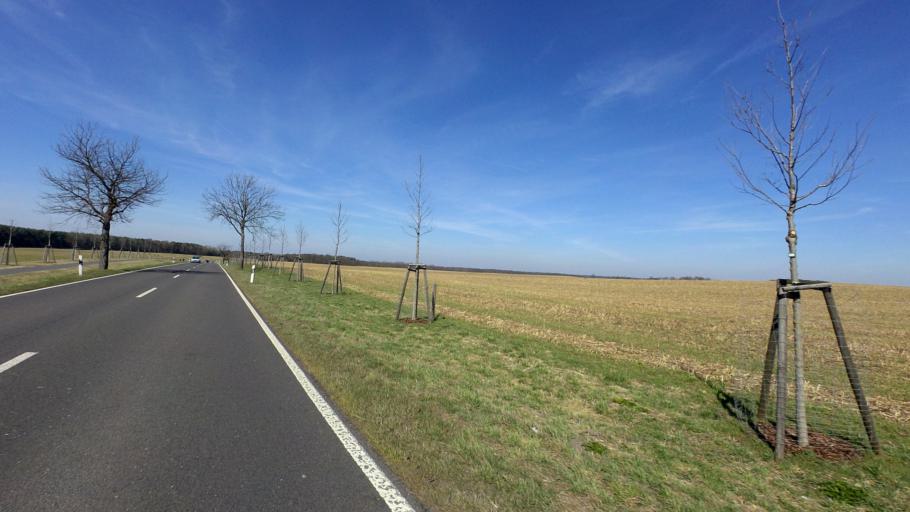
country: DE
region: Brandenburg
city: Furstenwalde
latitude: 52.3907
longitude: 14.0488
